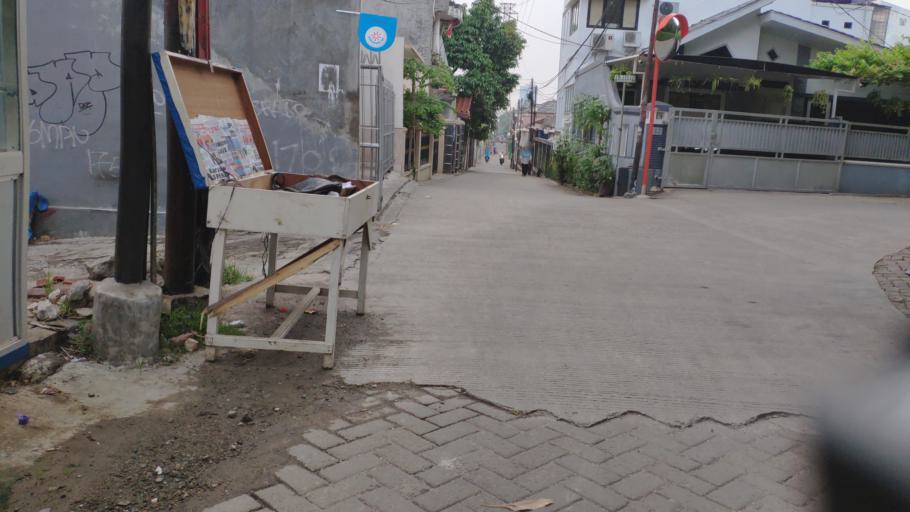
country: ID
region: West Java
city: Depok
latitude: -6.3135
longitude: 106.8280
